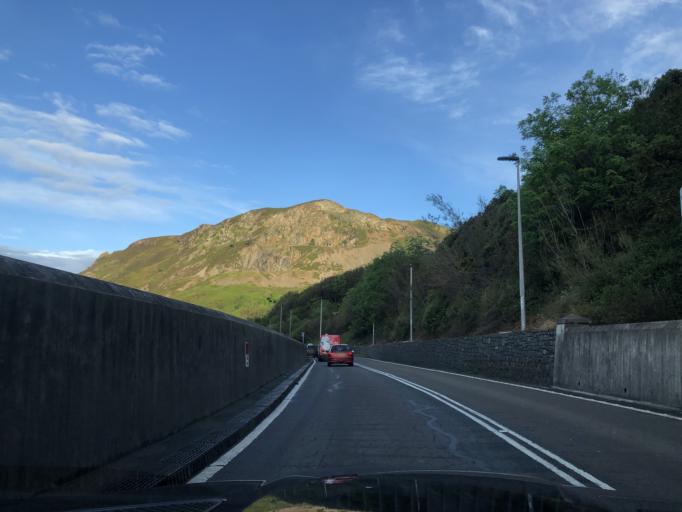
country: GB
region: Wales
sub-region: Conwy
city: Conwy
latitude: 53.2879
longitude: -3.8766
